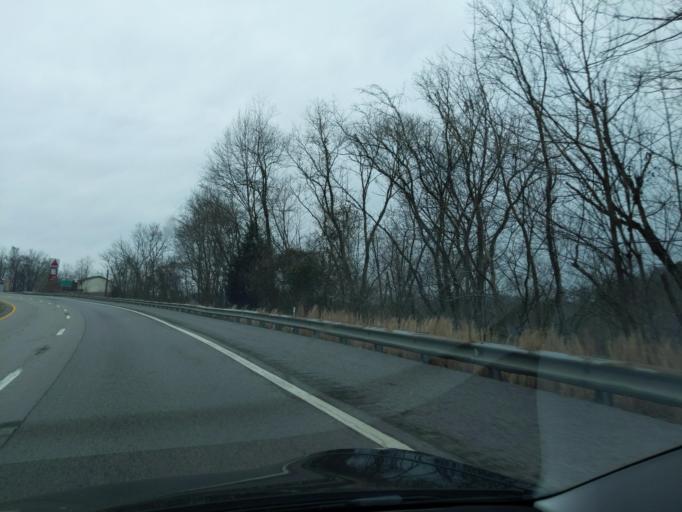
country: US
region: Kentucky
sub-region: Bell County
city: Middlesboro
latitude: 36.6402
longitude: -83.7041
